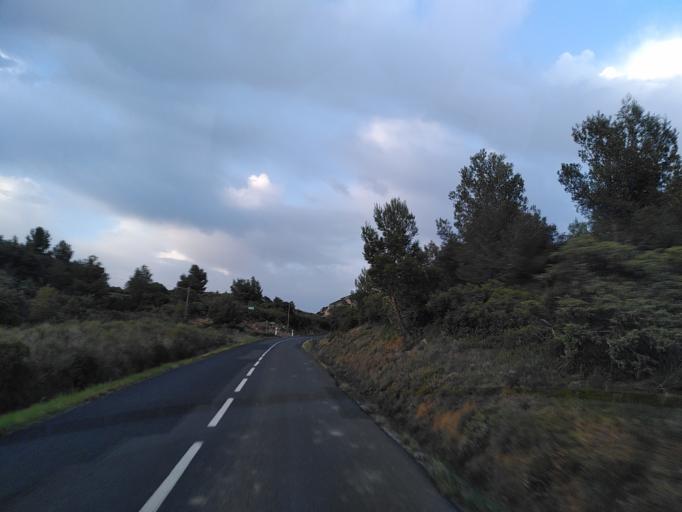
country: FR
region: Languedoc-Roussillon
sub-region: Departement des Pyrenees-Orientales
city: Estagel
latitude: 42.8210
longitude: 2.7100
